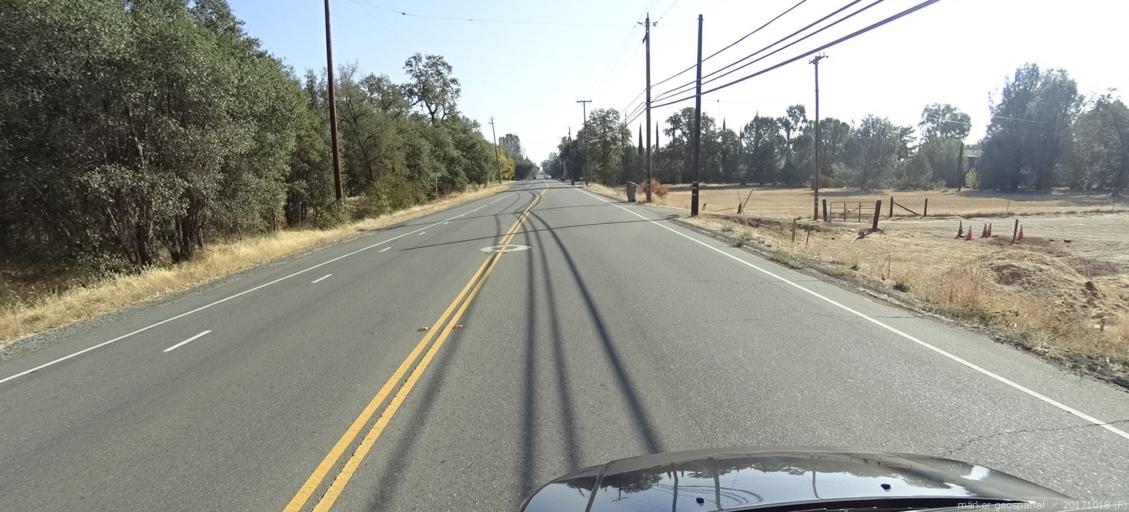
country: US
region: California
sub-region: Shasta County
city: Palo Cedro
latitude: 40.5347
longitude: -122.3137
